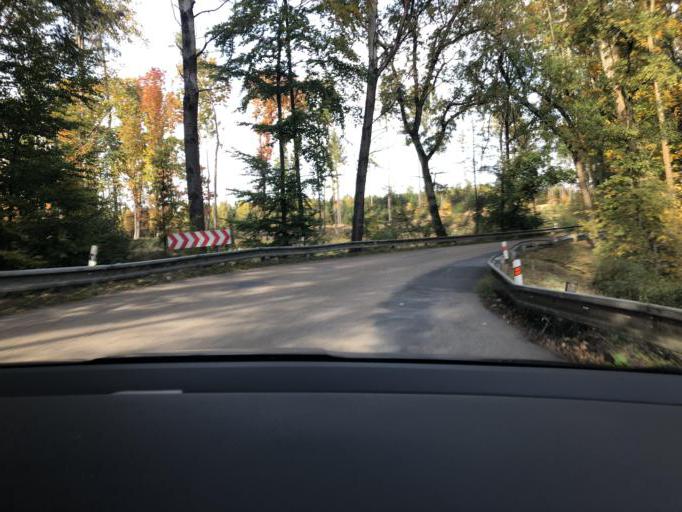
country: CZ
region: Central Bohemia
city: Postupice
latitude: 49.7768
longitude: 14.8008
